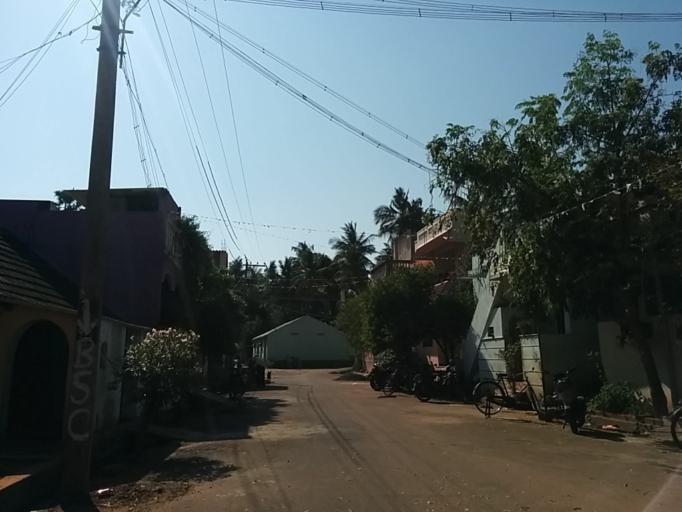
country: IN
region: Pondicherry
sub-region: Puducherry
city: Puducherry
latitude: 11.9622
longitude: 79.8267
